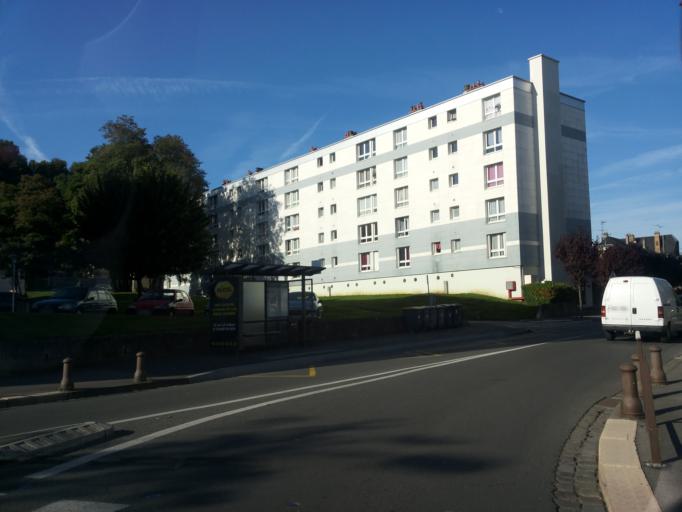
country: FR
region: Picardie
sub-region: Departement de l'Aisne
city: Laon
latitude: 49.5697
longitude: 3.6083
